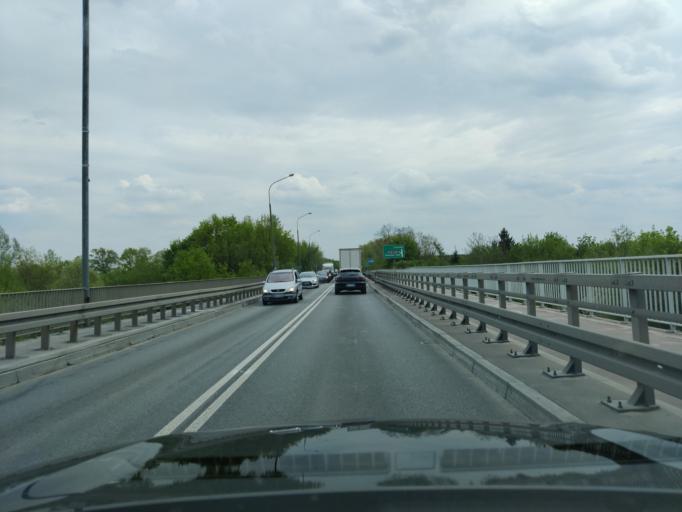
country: PL
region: Masovian Voivodeship
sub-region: Powiat wyszkowski
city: Wyszkow
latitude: 52.5903
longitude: 21.4609
